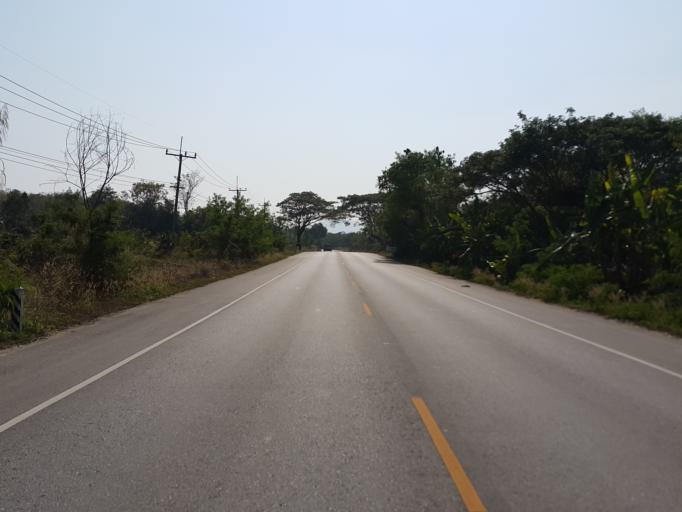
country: TH
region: Lampang
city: Mueang Pan
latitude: 18.8149
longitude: 99.5925
